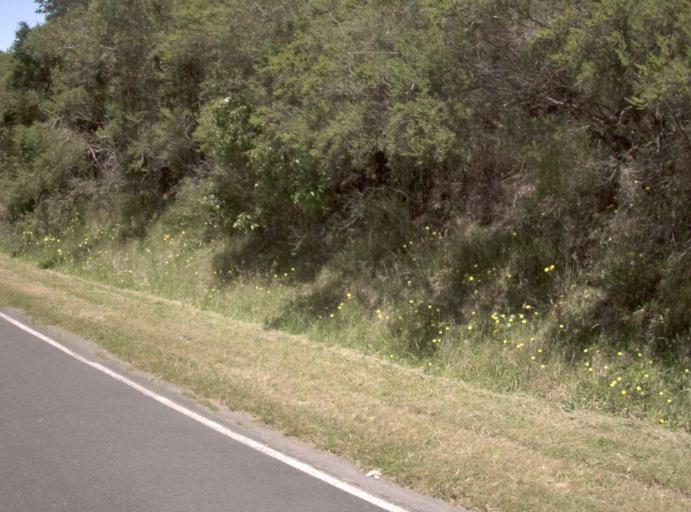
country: AU
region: Victoria
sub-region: Bass Coast
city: North Wonthaggi
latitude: -38.7764
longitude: 146.1623
